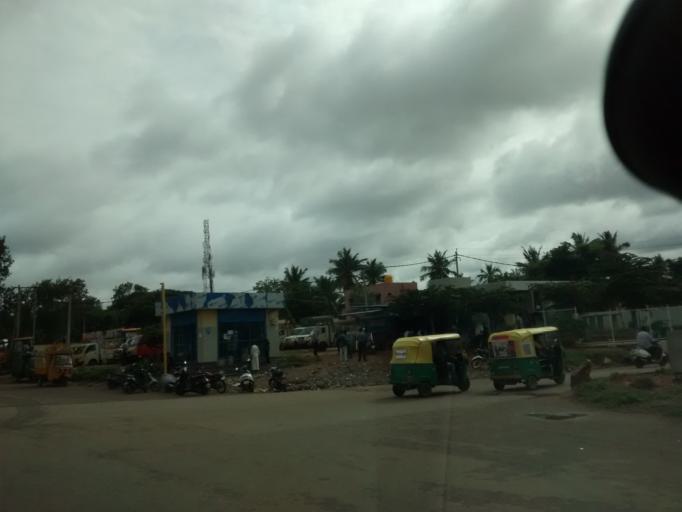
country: IN
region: Karnataka
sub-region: Tumkur
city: Tumkur
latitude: 13.3632
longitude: 77.1033
